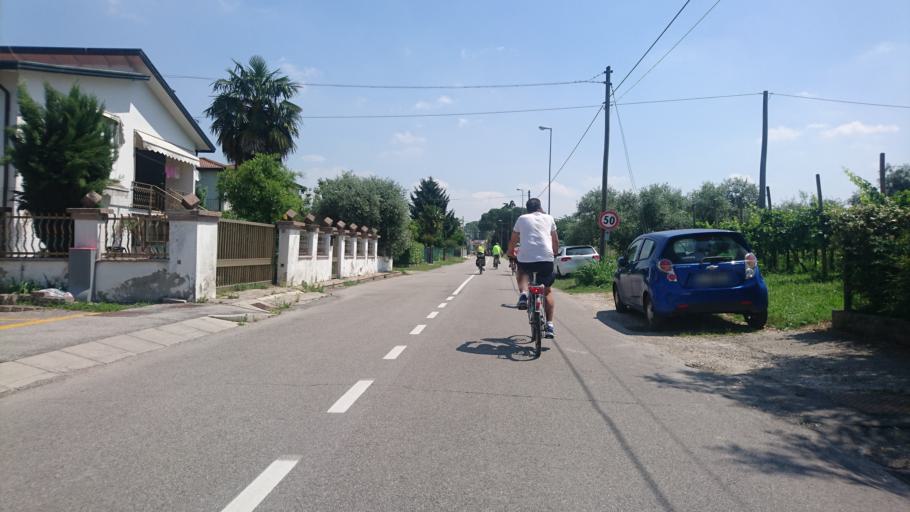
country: IT
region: Veneto
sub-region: Provincia di Venezia
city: Stra
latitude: 45.4015
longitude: 12.0180
